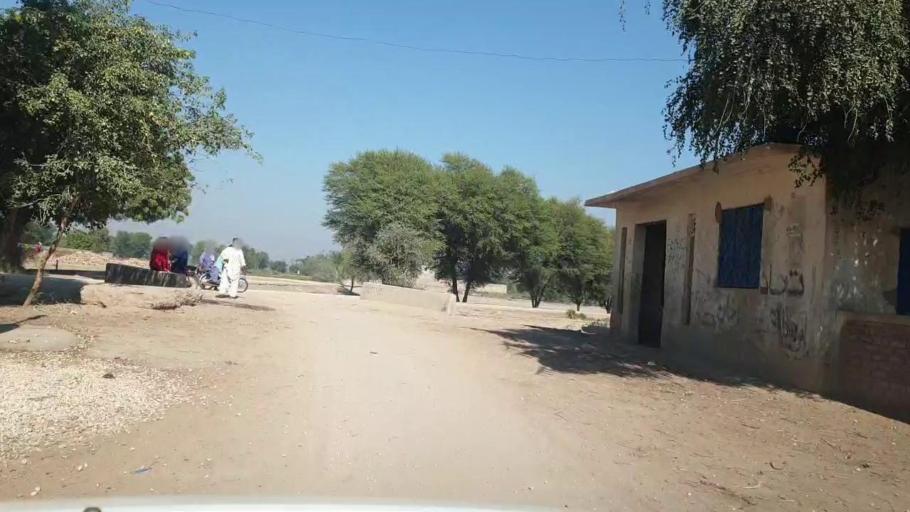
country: PK
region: Sindh
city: Johi
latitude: 26.6684
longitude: 67.7057
